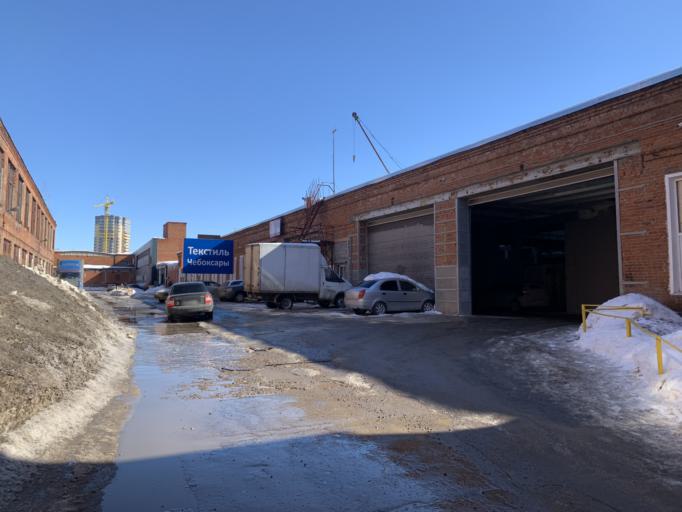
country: RU
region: Chuvashia
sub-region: Cheboksarskiy Rayon
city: Cheboksary
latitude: 56.1450
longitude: 47.2751
